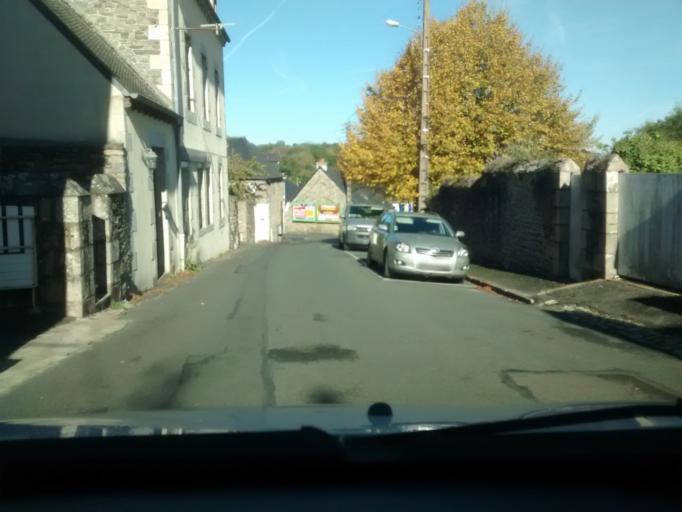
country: FR
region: Brittany
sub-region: Departement des Cotes-d'Armor
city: Treguier
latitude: 48.7895
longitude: -3.2295
